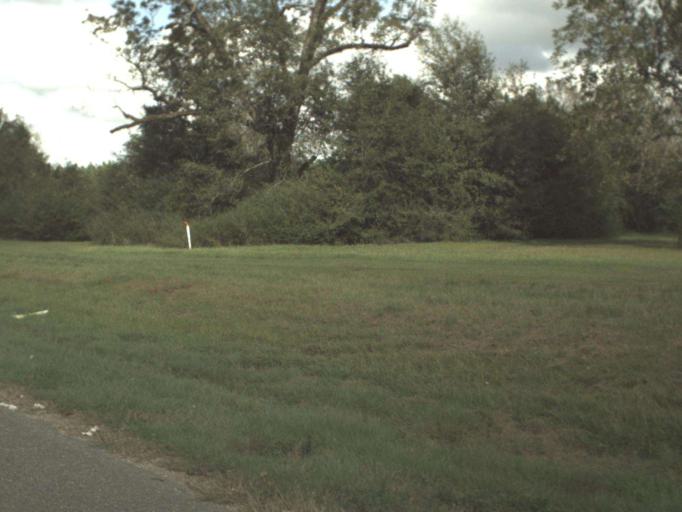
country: US
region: Florida
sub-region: Santa Rosa County
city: Point Baker
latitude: 30.7548
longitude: -87.0424
